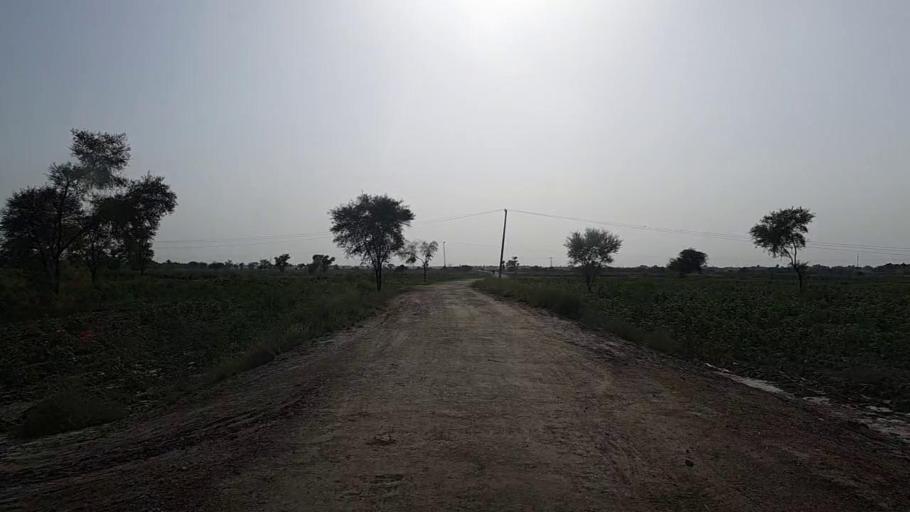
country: PK
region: Sindh
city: Pad Idan
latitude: 26.8531
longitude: 68.3046
